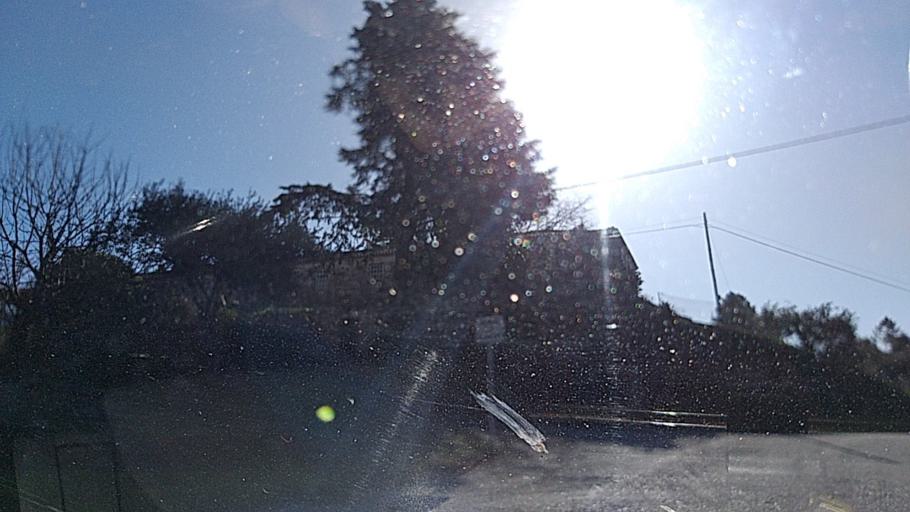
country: PT
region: Guarda
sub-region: Celorico da Beira
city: Celorico da Beira
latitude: 40.6862
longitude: -7.3984
